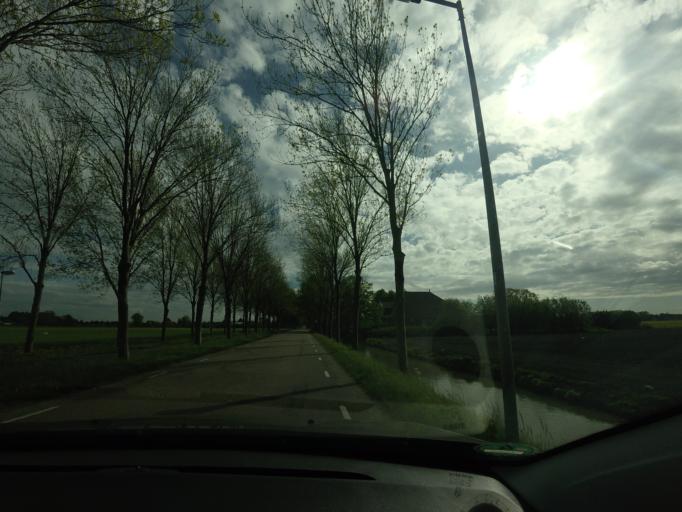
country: NL
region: North Holland
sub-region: Gemeente Beemster
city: Halfweg
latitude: 52.5370
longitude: 4.9059
